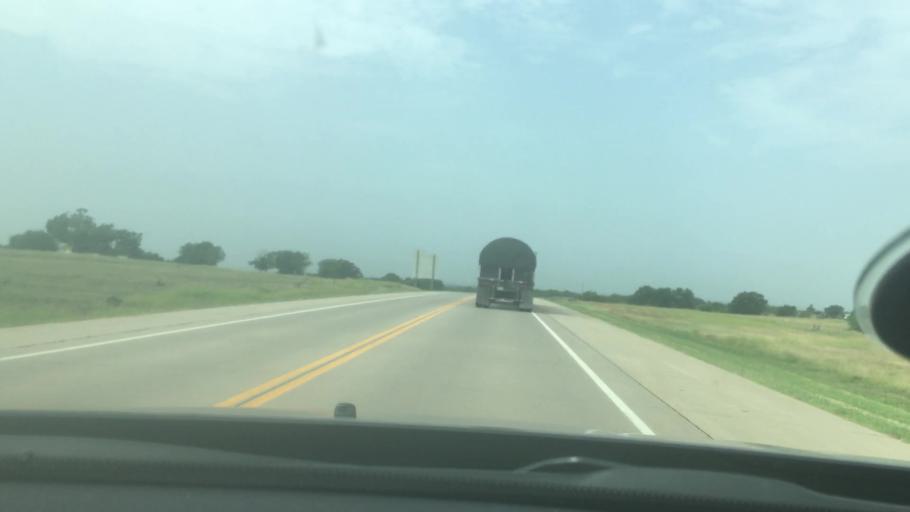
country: US
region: Oklahoma
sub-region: Murray County
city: Sulphur
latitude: 34.5384
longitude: -96.9888
